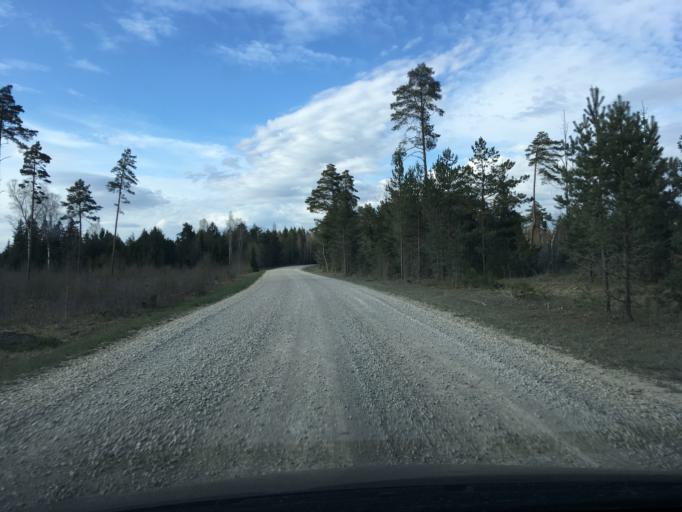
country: EE
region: Raplamaa
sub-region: Maerjamaa vald
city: Marjamaa
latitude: 58.9651
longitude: 24.3314
